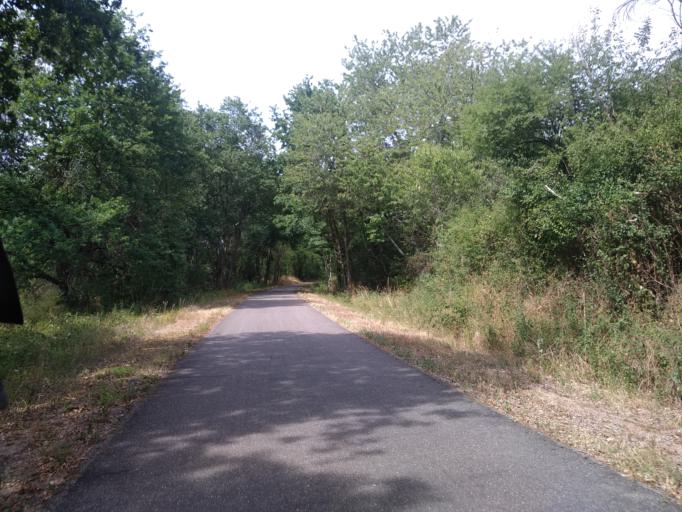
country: FR
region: Auvergne
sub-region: Departement de l'Allier
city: Diou
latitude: 46.5495
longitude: 3.7414
